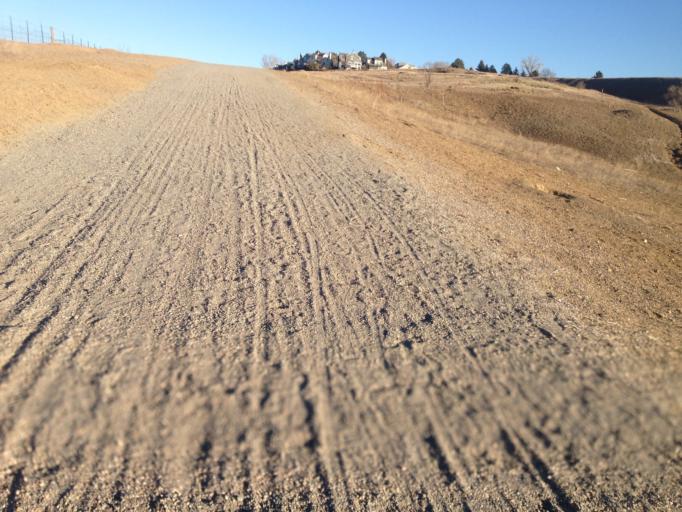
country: US
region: Colorado
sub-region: Broomfield County
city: Broomfield
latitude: 39.9360
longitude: -105.1015
